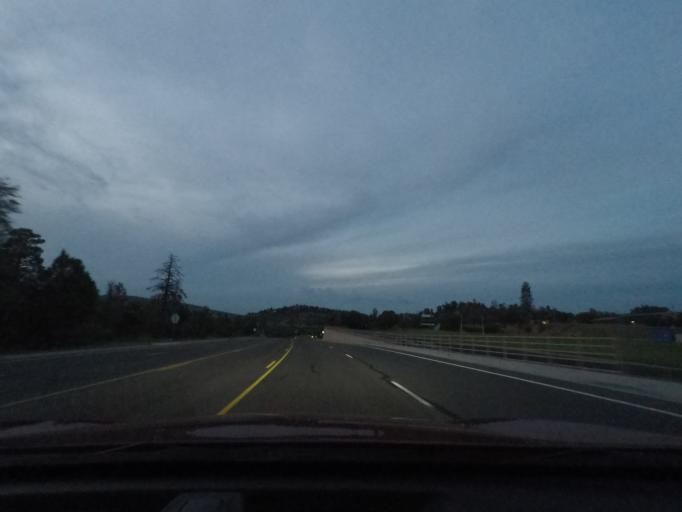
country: US
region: Arizona
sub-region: Yavapai County
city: Prescott
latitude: 34.5736
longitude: -112.4988
